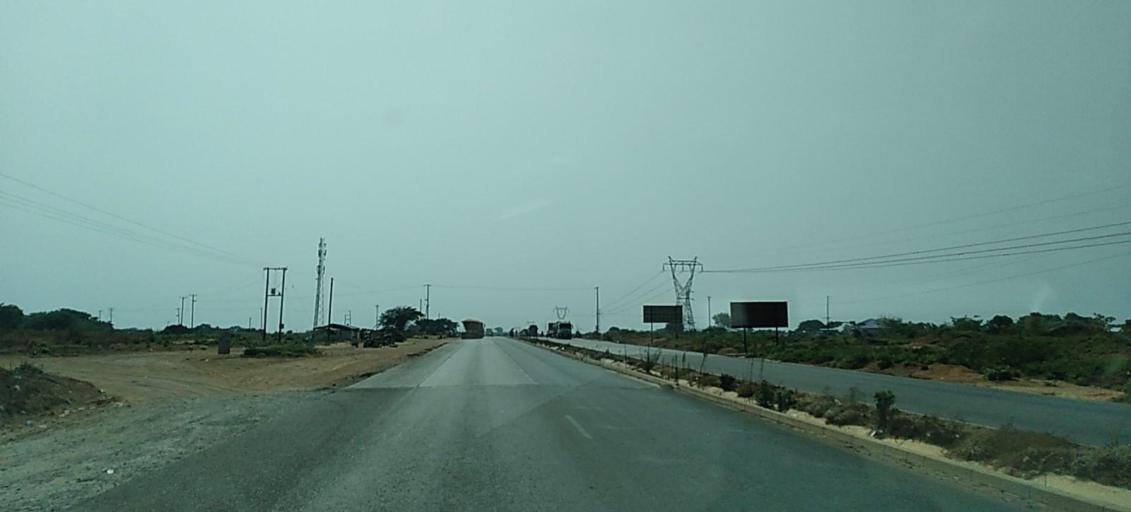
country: ZM
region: Copperbelt
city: Chingola
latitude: -12.5665
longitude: 27.8970
